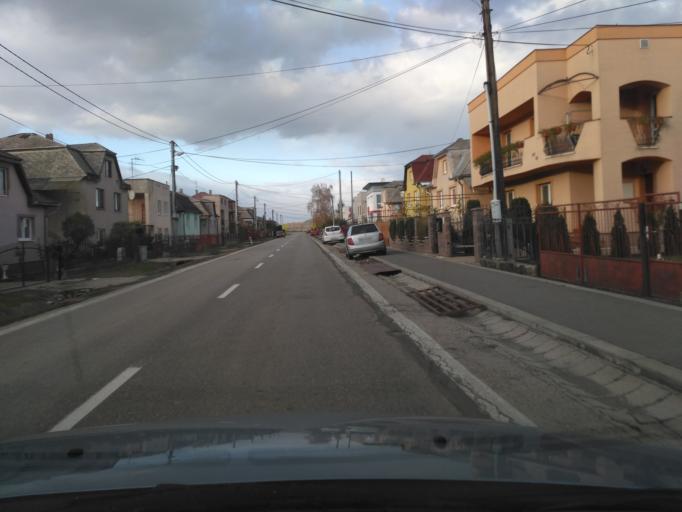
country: HU
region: Borsod-Abauj-Zemplen
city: Satoraljaujhely
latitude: 48.4086
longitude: 21.6681
